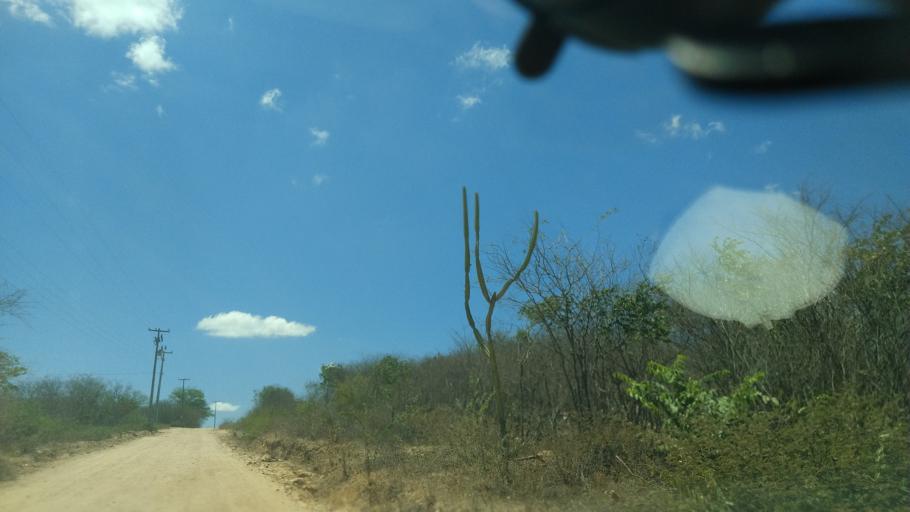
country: BR
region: Rio Grande do Norte
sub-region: Cerro Cora
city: Cerro Cora
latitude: -6.0244
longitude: -36.3344
